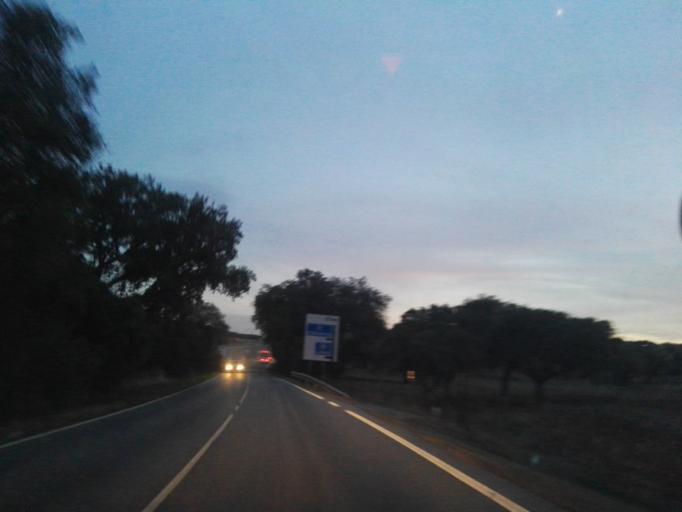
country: PT
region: Portalegre
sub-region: Elvas
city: Elvas
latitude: 38.9127
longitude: -7.1817
